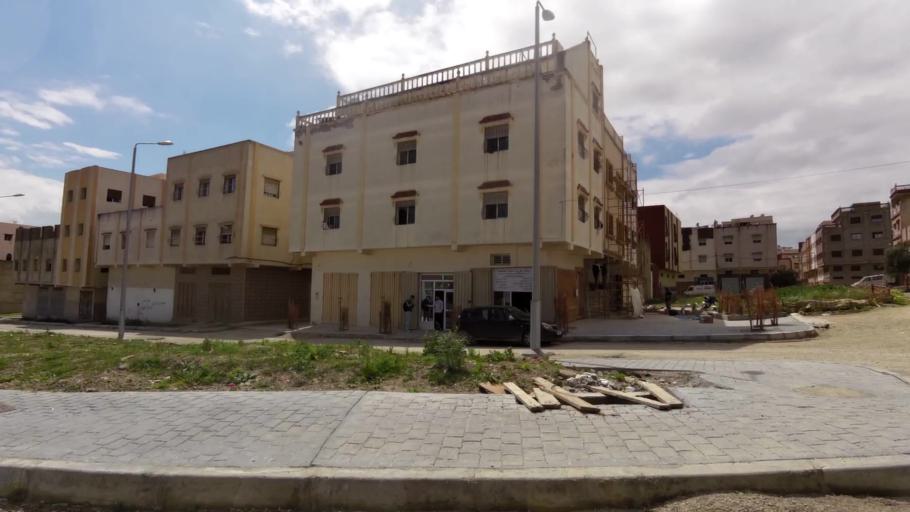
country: MA
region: Tanger-Tetouan
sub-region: Tanger-Assilah
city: Tangier
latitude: 35.7590
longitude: -5.8482
